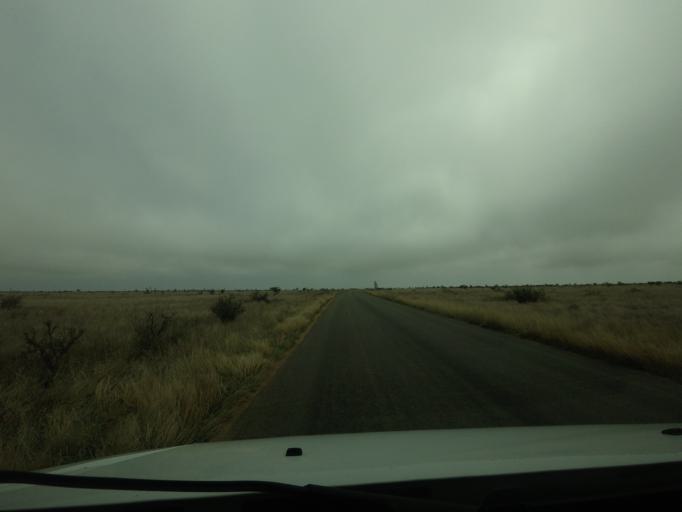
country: ZA
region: Limpopo
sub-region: Mopani District Municipality
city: Phalaborwa
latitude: -24.2193
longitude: 31.7199
